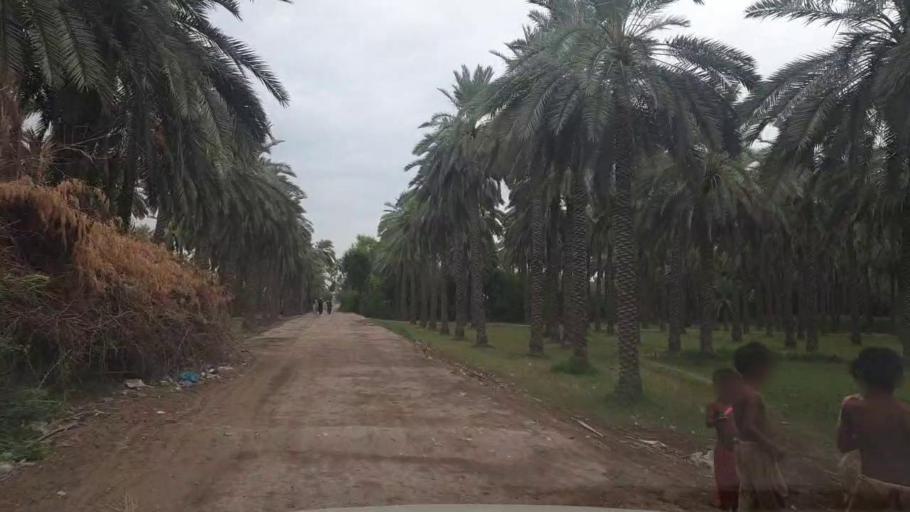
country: PK
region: Sindh
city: Khairpur
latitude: 27.5945
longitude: 68.8140
